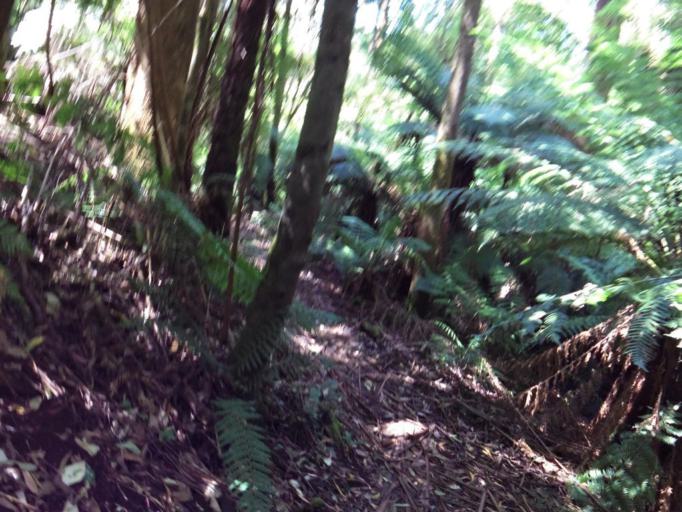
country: AU
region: Victoria
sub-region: Yarra Ranges
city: Mount Dandenong
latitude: -37.8339
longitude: 145.3662
